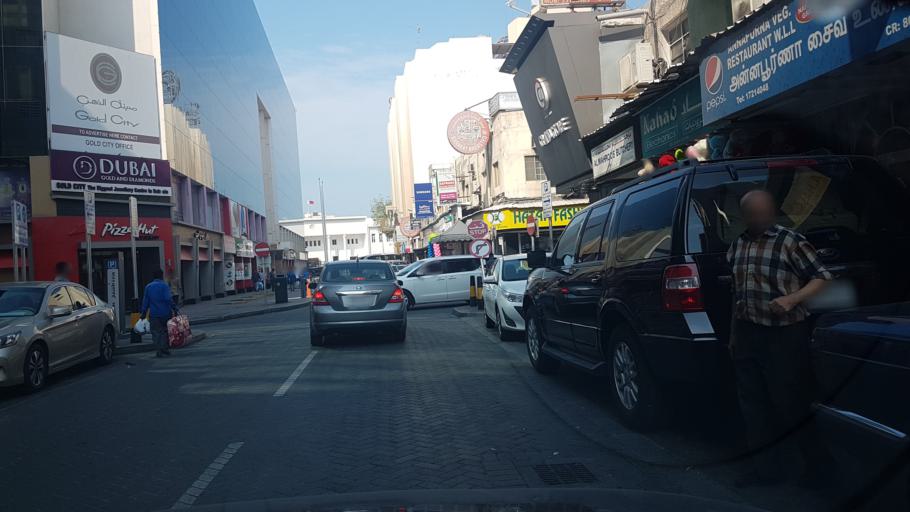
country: BH
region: Manama
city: Manama
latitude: 26.2317
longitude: 50.5738
